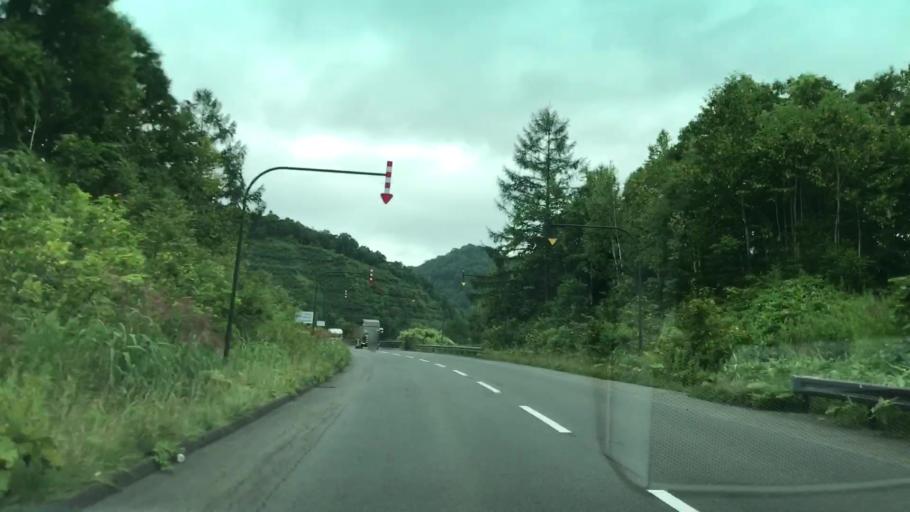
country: JP
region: Hokkaido
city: Otaru
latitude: 42.9942
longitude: 140.8771
